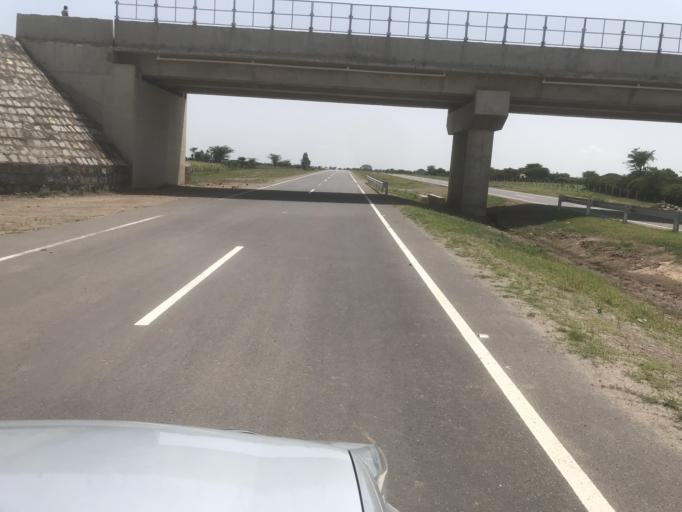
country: ET
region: Oromiya
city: Ziway
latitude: 8.2516
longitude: 38.8898
